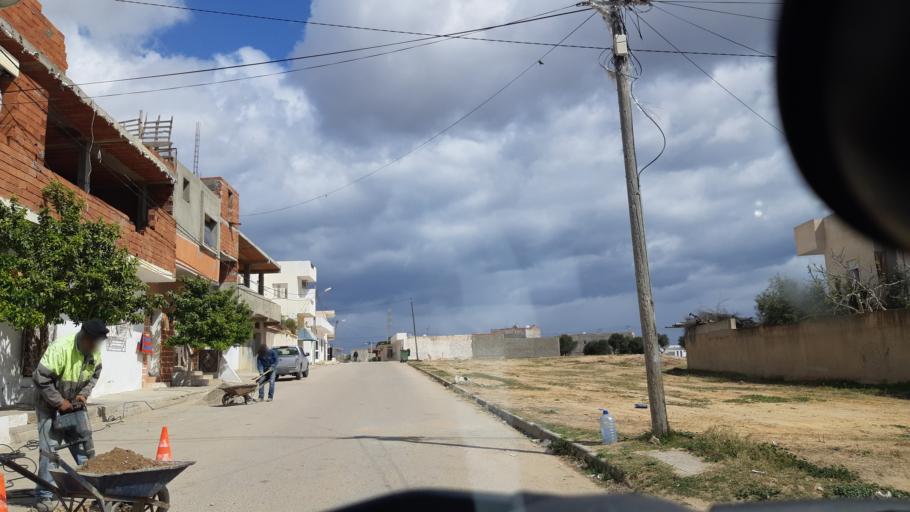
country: TN
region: Susah
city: Akouda
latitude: 35.8814
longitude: 10.5377
